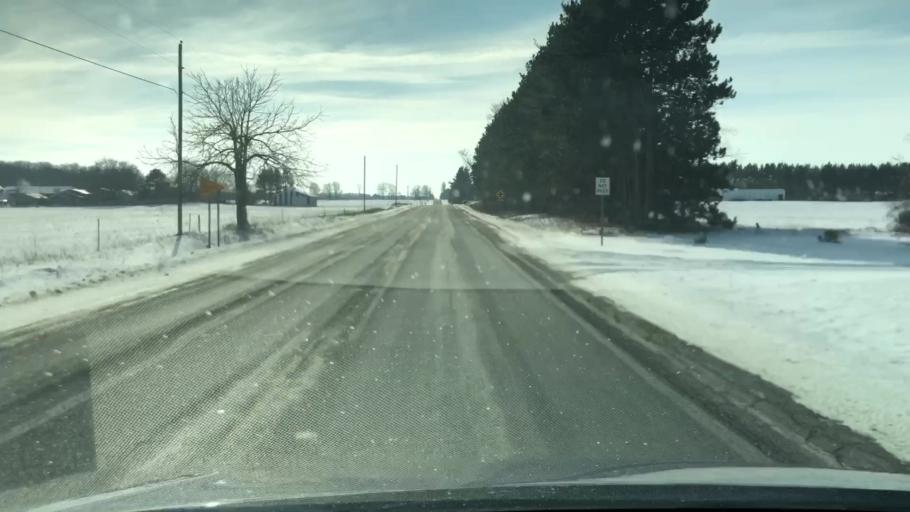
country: US
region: Michigan
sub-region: Kalkaska County
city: Kalkaska
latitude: 44.7309
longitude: -85.0527
